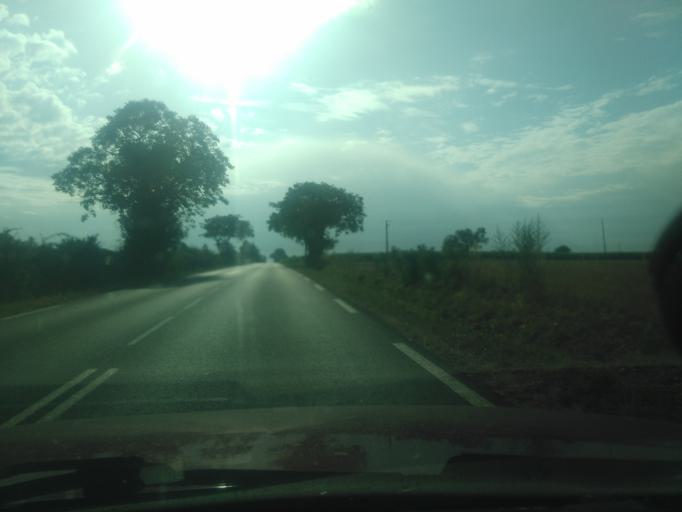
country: FR
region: Pays de la Loire
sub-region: Departement de la Vendee
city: Bazoges-en-Pareds
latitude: 46.6803
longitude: -0.9652
